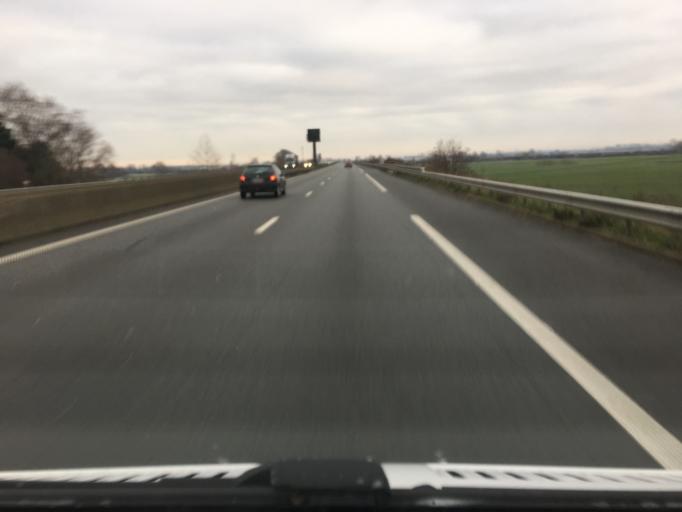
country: FR
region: Nord-Pas-de-Calais
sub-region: Departement du Nord
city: Meteren
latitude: 50.7284
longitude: 2.7135
